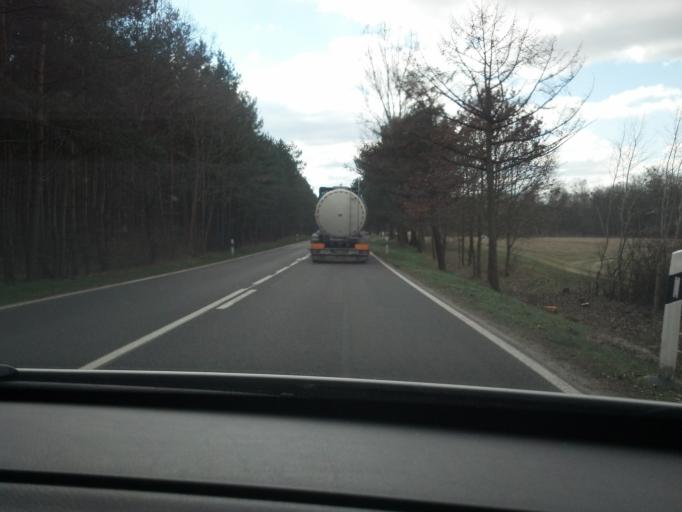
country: DE
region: Mecklenburg-Vorpommern
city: Neustrelitz
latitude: 53.2981
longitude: 13.0406
